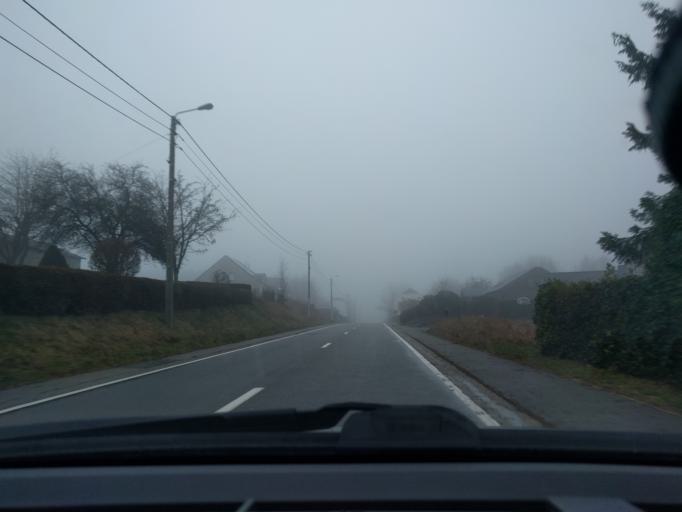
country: BE
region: Wallonia
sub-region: Province du Luxembourg
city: Gouvy
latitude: 50.1925
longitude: 5.9594
